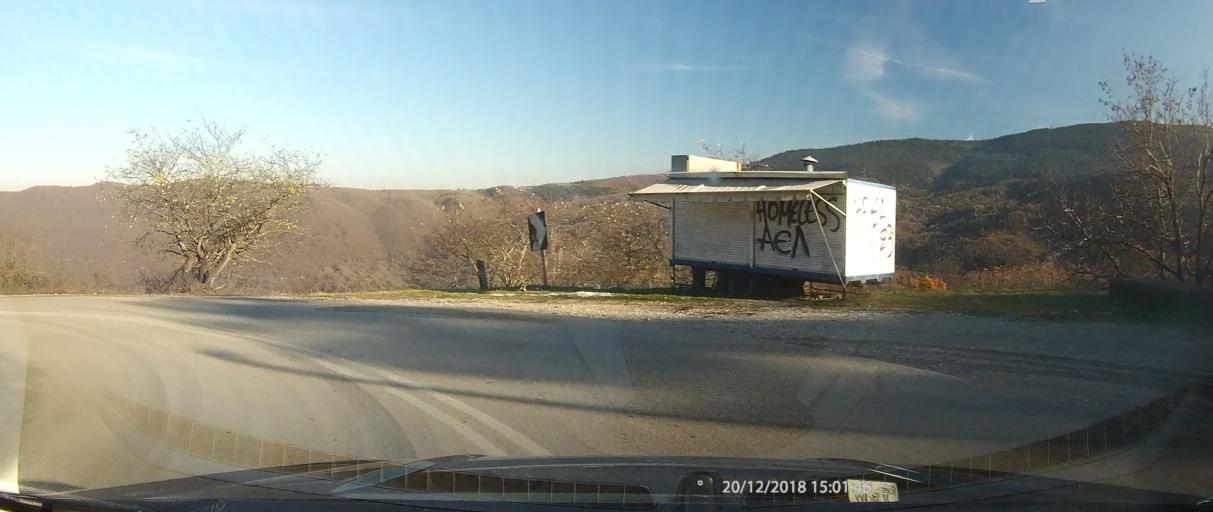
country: GR
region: Central Greece
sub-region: Nomos Evrytanias
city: Karpenisi
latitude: 38.9092
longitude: 21.9182
